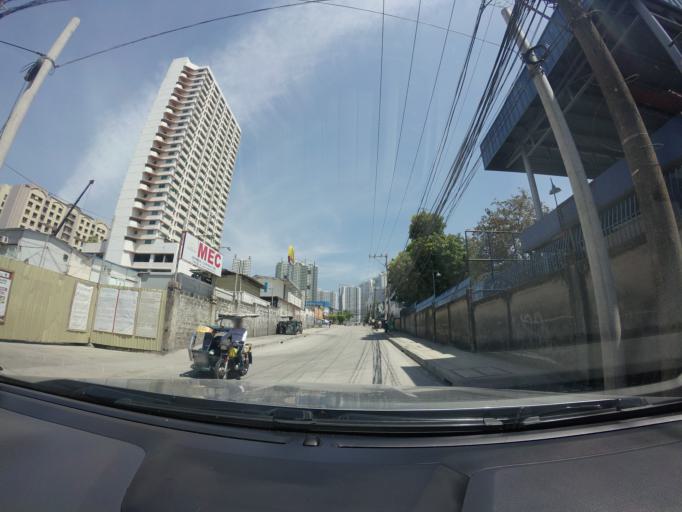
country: PH
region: Metro Manila
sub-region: Pasig
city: Pasig City
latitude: 14.5718
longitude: 121.0551
